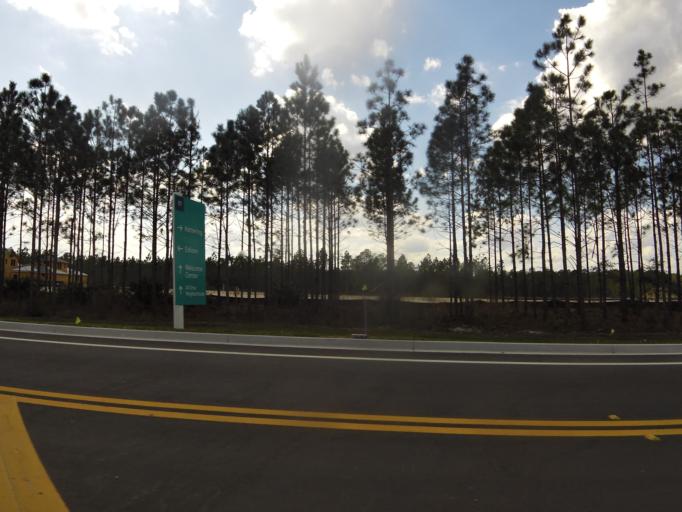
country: US
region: Florida
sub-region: Saint Johns County
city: Palm Valley
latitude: 30.1978
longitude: -81.5078
